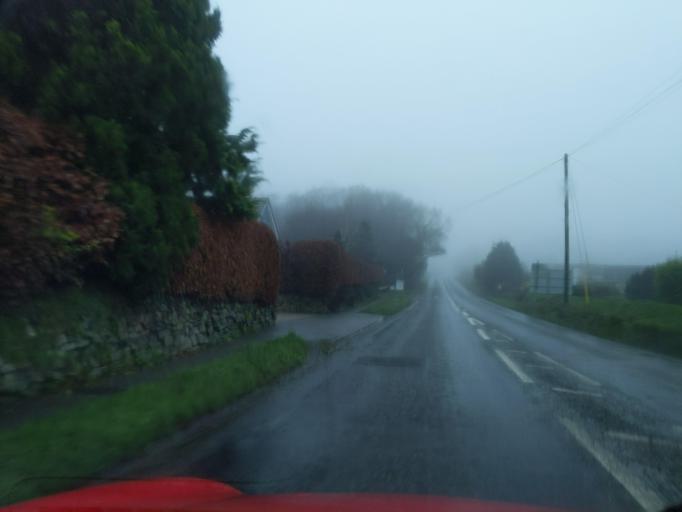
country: GB
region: England
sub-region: Cornwall
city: Callington
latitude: 50.5211
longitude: -4.3170
